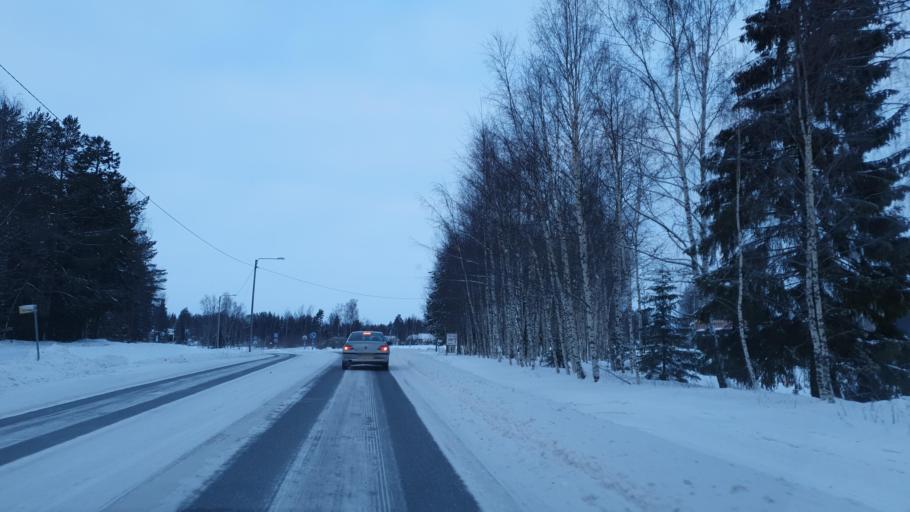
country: FI
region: Northern Ostrobothnia
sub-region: Oulu
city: Haukipudas
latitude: 65.2065
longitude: 25.3316
